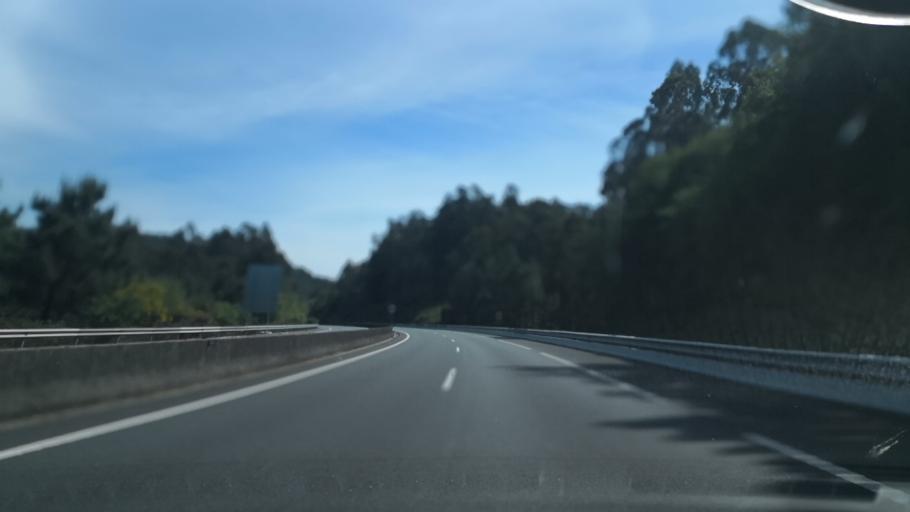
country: ES
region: Galicia
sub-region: Provincia de Pontevedra
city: Portas
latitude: 42.5936
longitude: -8.6781
